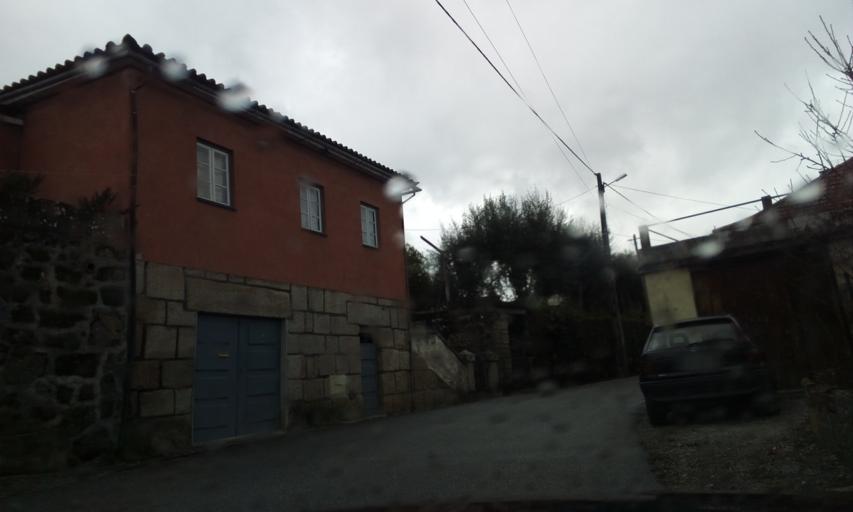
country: PT
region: Viseu
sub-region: Nelas
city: Nelas
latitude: 40.5999
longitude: -7.8424
